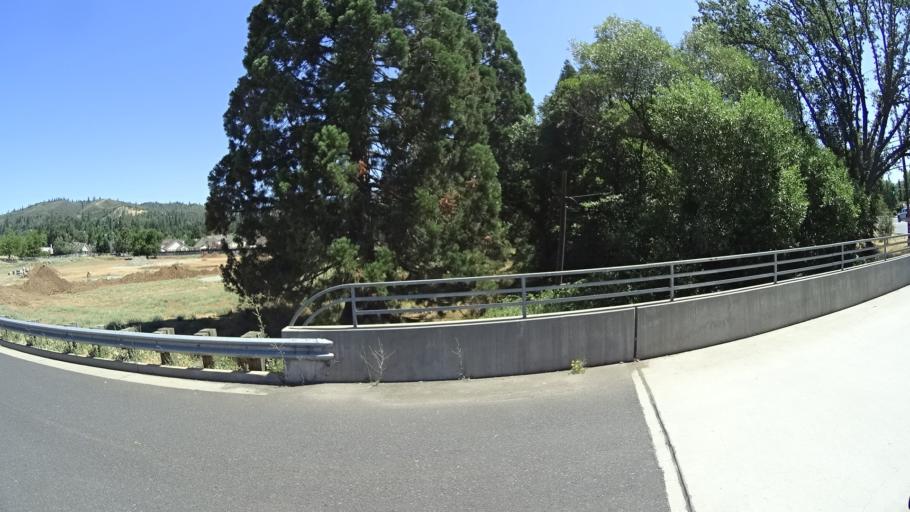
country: US
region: California
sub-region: Calaveras County
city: Murphys
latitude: 38.1396
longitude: -120.4568
